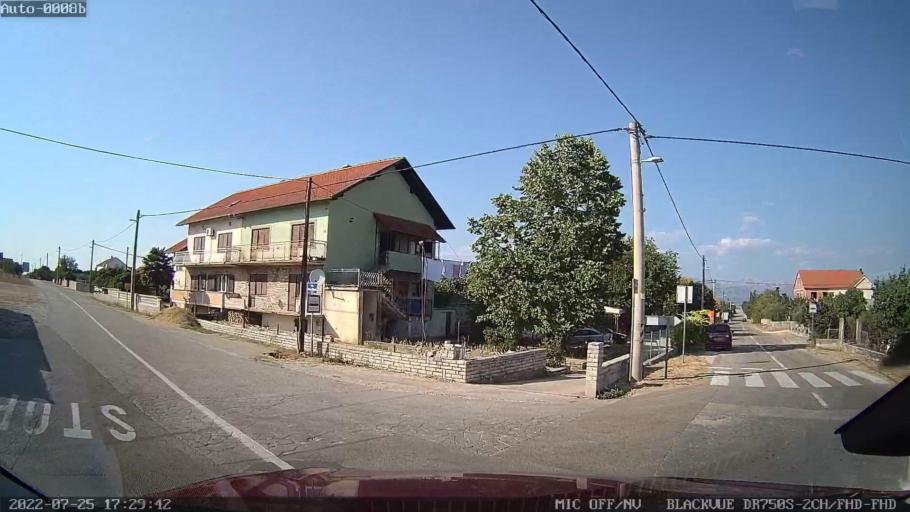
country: HR
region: Zadarska
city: Pridraga
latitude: 44.1608
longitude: 15.5144
